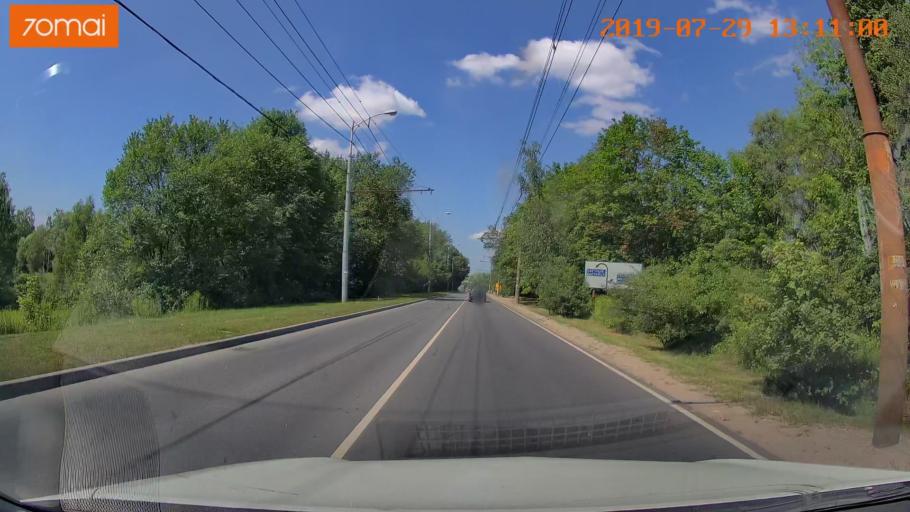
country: RU
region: Kaliningrad
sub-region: Gorod Kaliningrad
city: Kaliningrad
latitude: 54.7176
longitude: 20.3943
